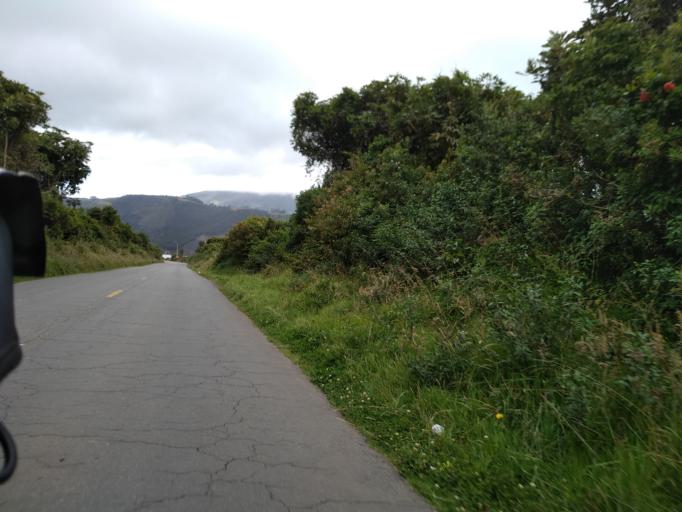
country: EC
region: Carchi
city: El Angel
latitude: 0.6277
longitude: -77.9326
